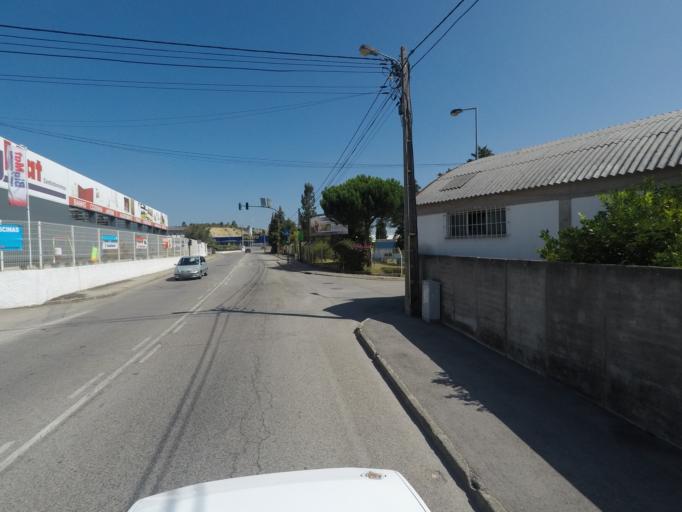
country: PT
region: Coimbra
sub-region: Coimbra
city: Coimbra
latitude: 40.2408
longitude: -8.4347
